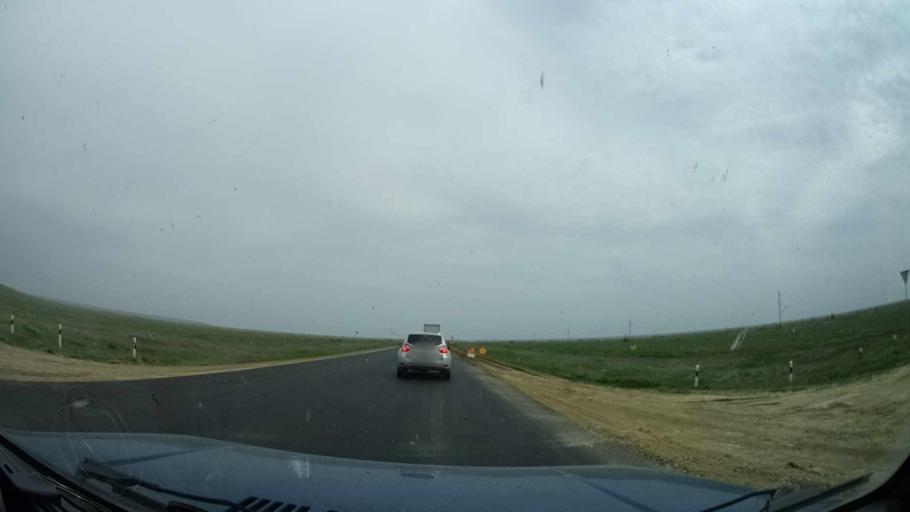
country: RU
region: Kalmykiya
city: Malyye Derbety
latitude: 47.8989
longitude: 44.6156
